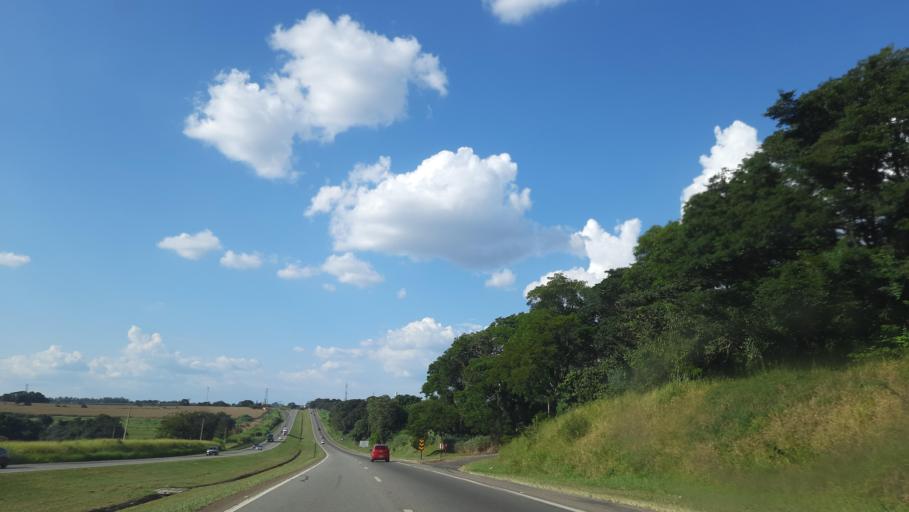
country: BR
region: Sao Paulo
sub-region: Mogi-Mirim
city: Mogi Mirim
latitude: -22.5017
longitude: -46.9848
